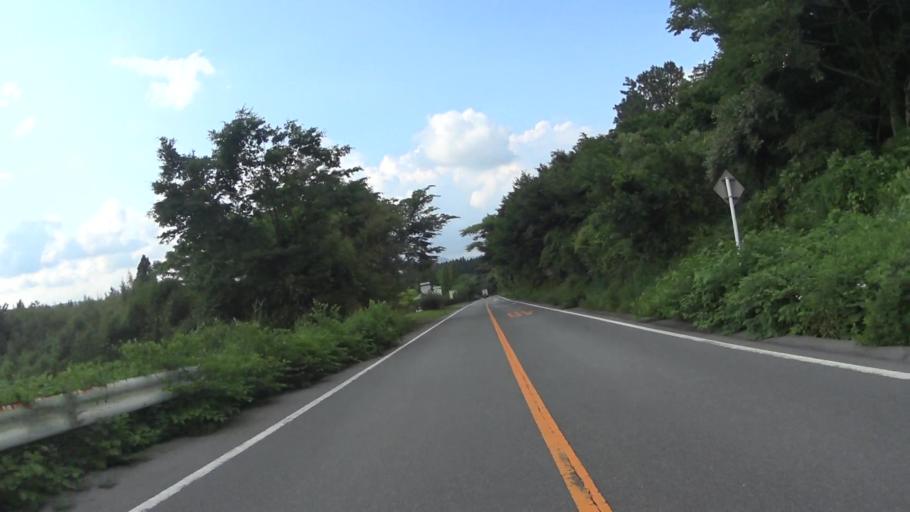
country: JP
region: Kumamoto
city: Aso
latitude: 32.8959
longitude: 131.0178
